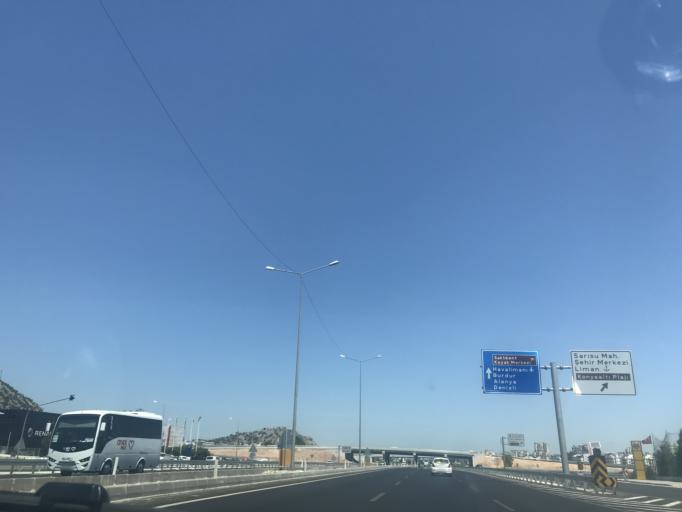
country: TR
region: Antalya
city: Cakirlar
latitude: 36.8441
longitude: 30.5991
